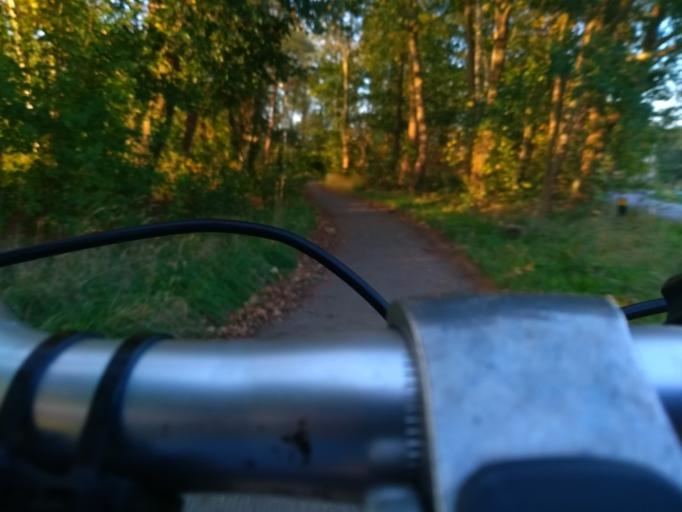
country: NL
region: Drenthe
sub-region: Gemeente Assen
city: Assen
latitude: 52.9755
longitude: 6.5809
